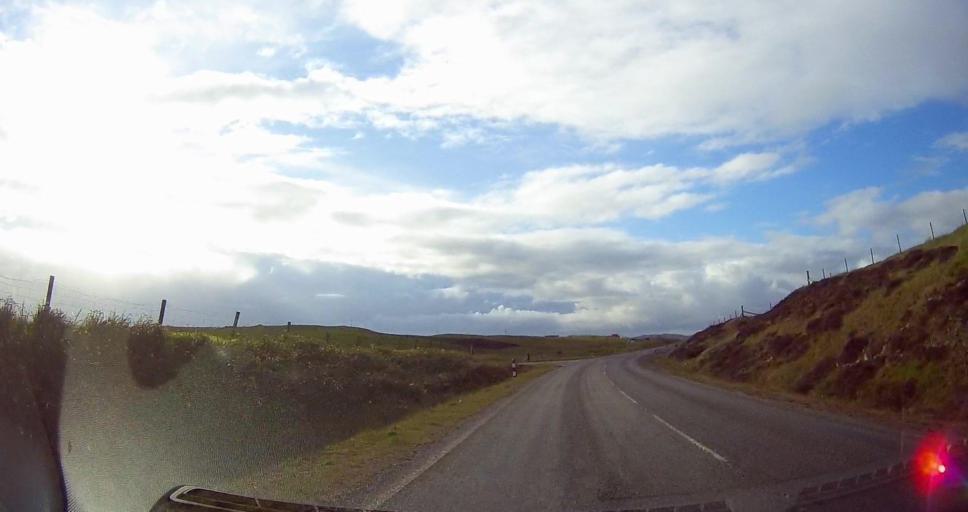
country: GB
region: Scotland
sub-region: Shetland Islands
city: Lerwick
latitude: 60.3725
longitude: -1.3354
